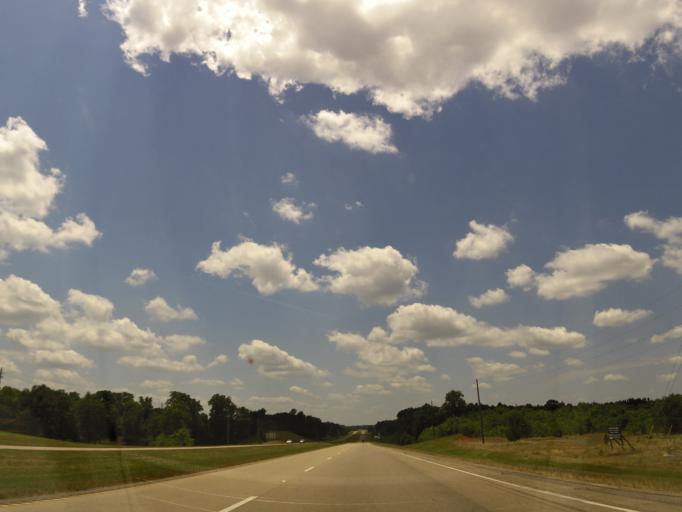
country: US
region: Mississippi
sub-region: Pontotoc County
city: Pontotoc
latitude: 34.2858
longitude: -89.0325
